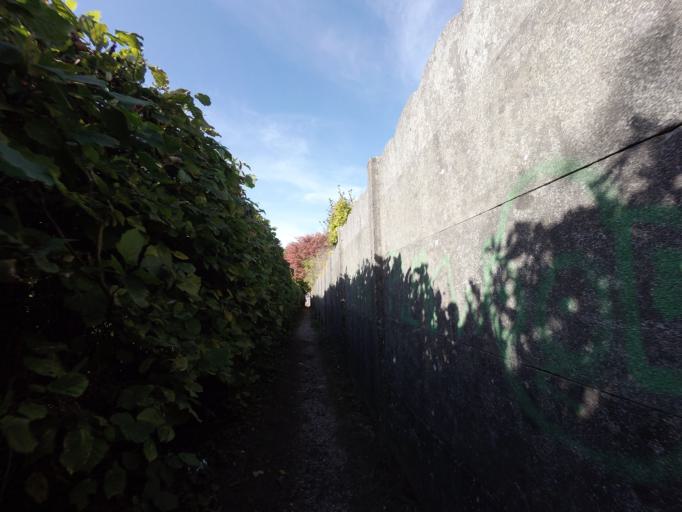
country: BE
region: Flanders
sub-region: Provincie Vlaams-Brabant
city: Kortenberg
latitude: 50.9029
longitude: 4.5636
